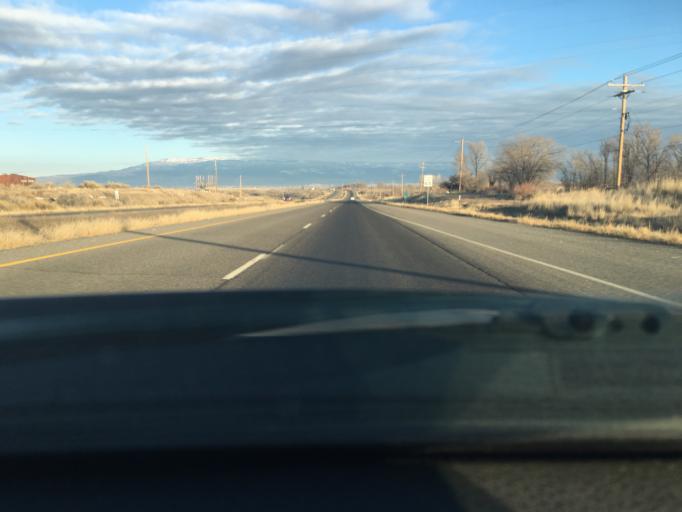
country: US
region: Colorado
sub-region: Montrose County
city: Olathe
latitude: 38.6527
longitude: -107.9910
